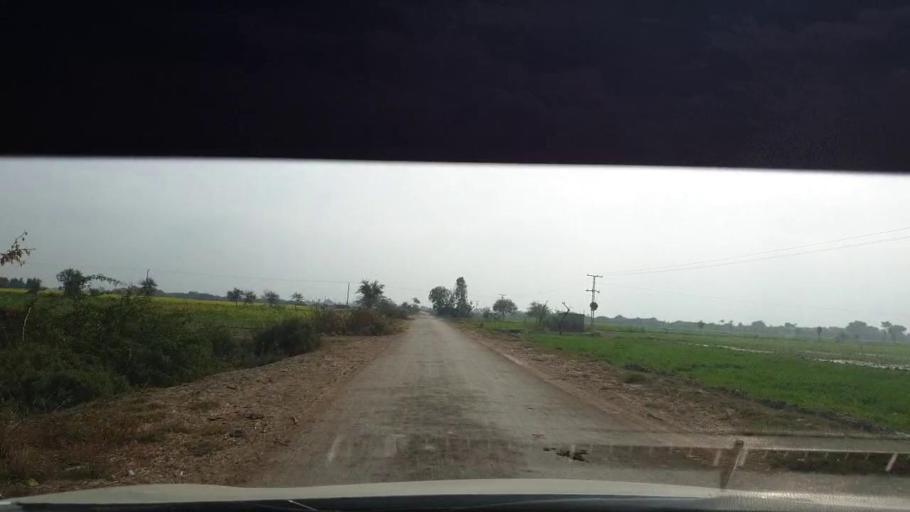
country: PK
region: Sindh
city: Berani
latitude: 25.7704
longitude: 68.8761
